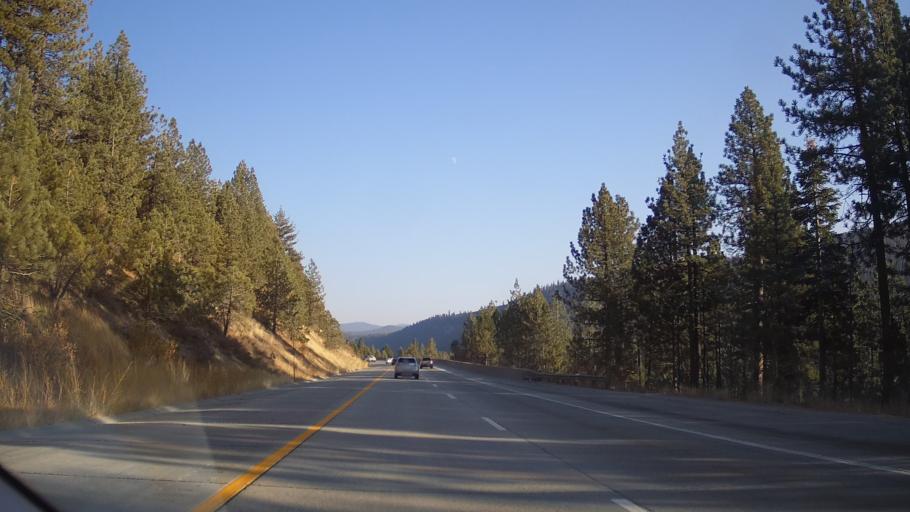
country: US
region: California
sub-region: Nevada County
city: Truckee
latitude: 39.3282
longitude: -120.2789
